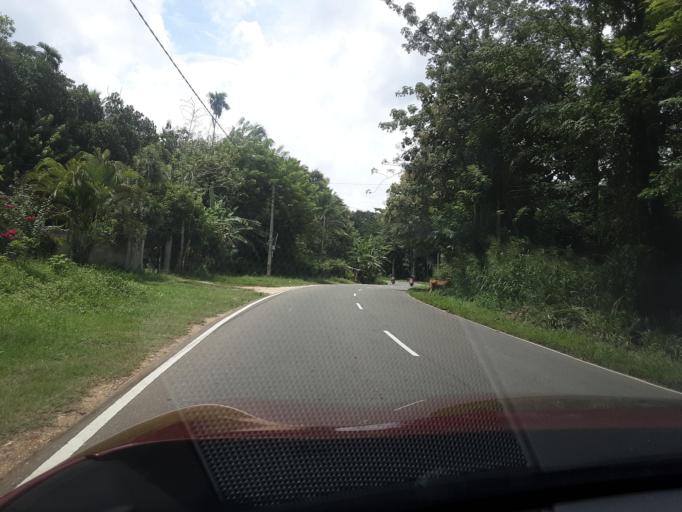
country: LK
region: Uva
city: Monaragala
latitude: 6.8923
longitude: 81.2923
